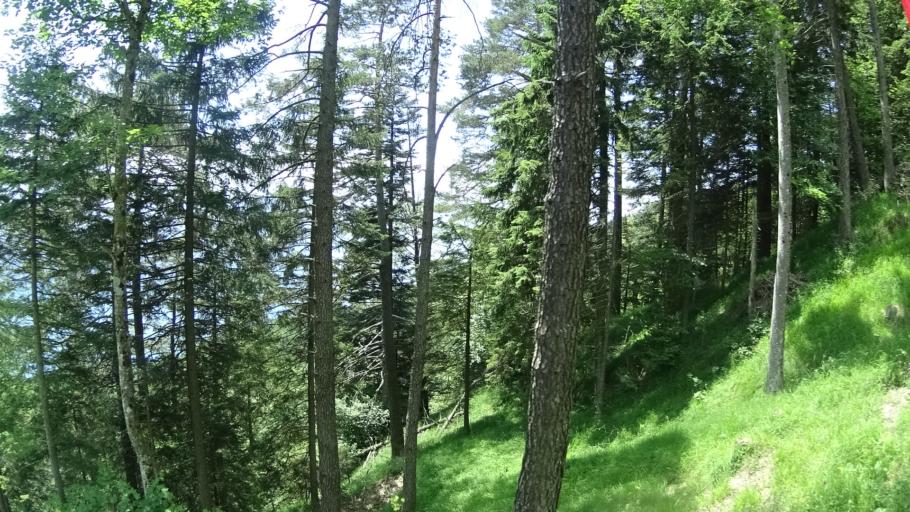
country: CH
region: Lucerne
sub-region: Lucerne-Land District
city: Vitznau
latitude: 47.0318
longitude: 8.4787
